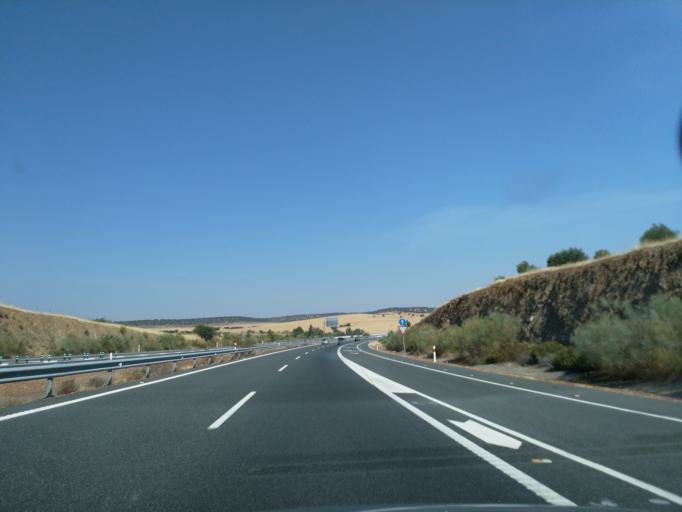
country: ES
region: Extremadura
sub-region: Provincia de Badajoz
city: Aljucen
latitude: 39.0420
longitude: -6.3389
